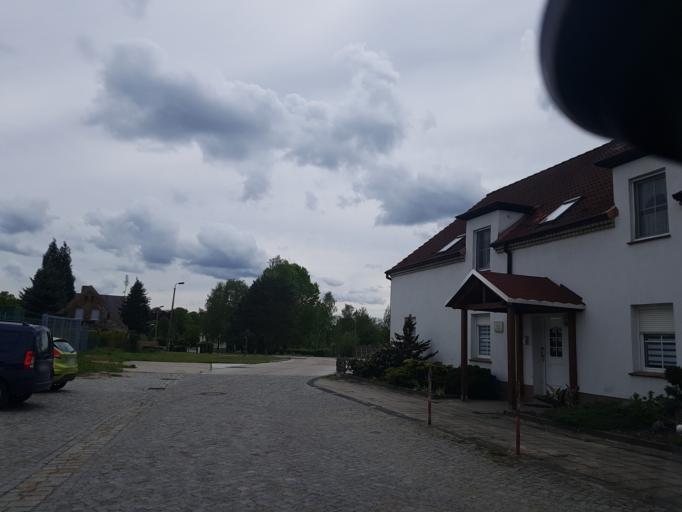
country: DE
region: Saxony
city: Gross Duben
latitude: 51.6054
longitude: 14.5719
